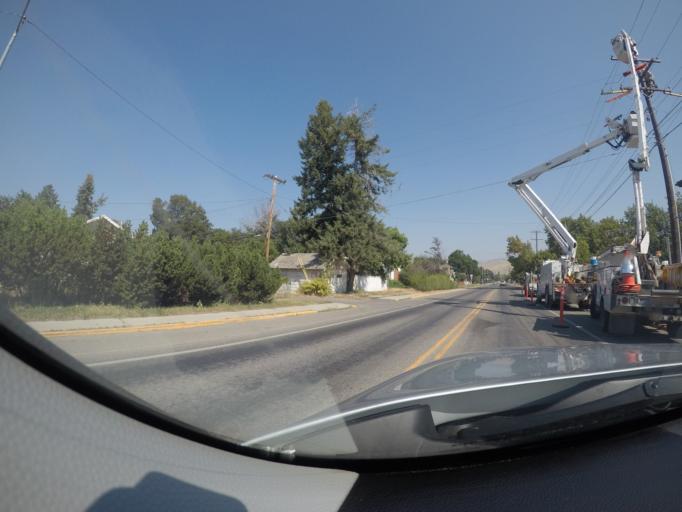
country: US
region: Montana
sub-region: Missoula County
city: Missoula
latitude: 46.8624
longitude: -113.9893
